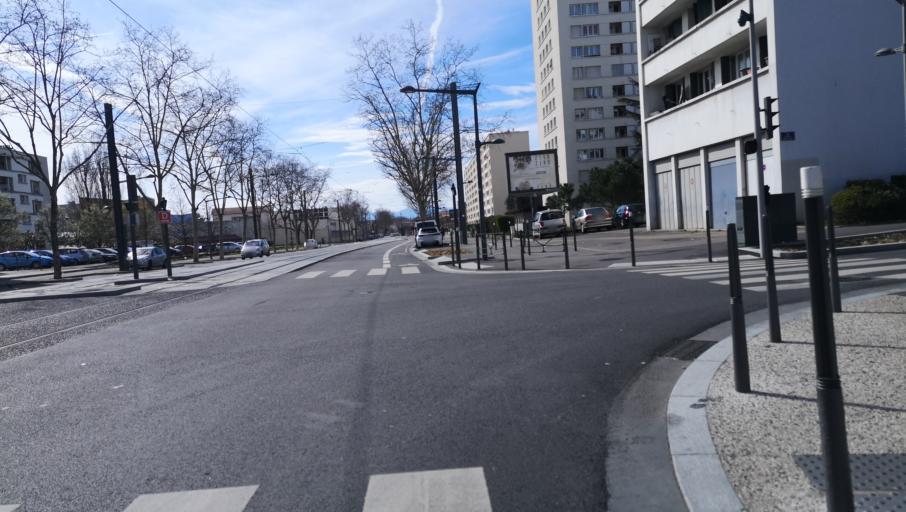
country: FR
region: Rhone-Alpes
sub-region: Departement du Rhone
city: Saint-Fons
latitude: 45.7289
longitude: 4.8660
